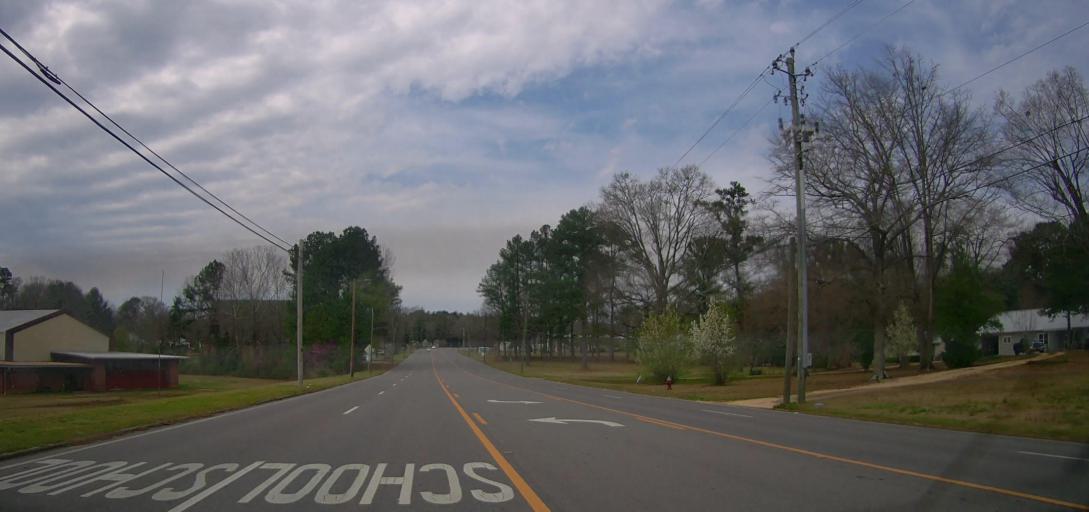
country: US
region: Alabama
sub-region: Marion County
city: Guin
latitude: 33.9756
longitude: -87.9156
